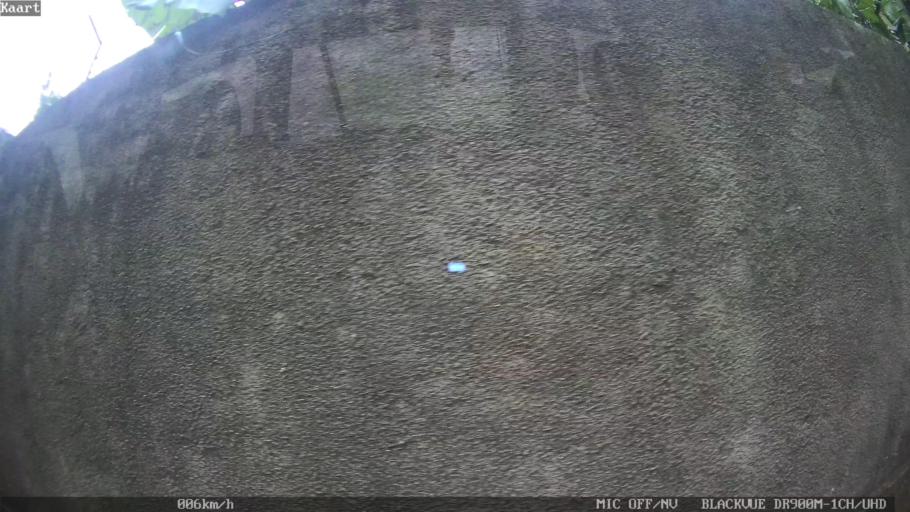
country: ID
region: Lampung
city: Kedaton
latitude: -5.4029
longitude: 105.2714
